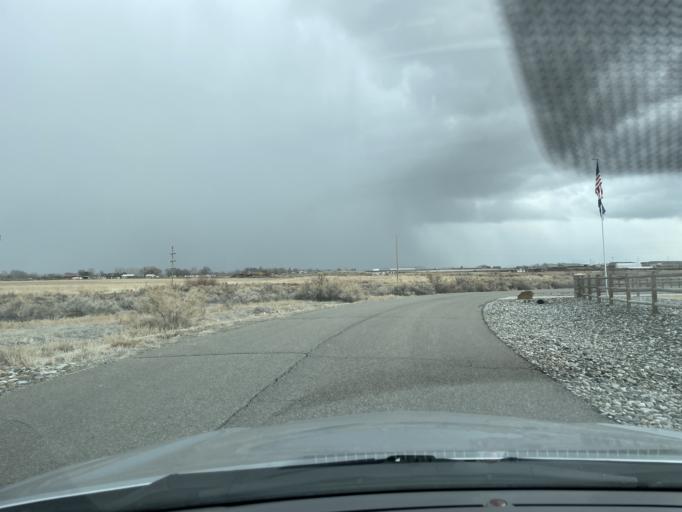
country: US
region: Colorado
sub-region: Mesa County
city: Loma
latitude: 39.2177
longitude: -108.8053
